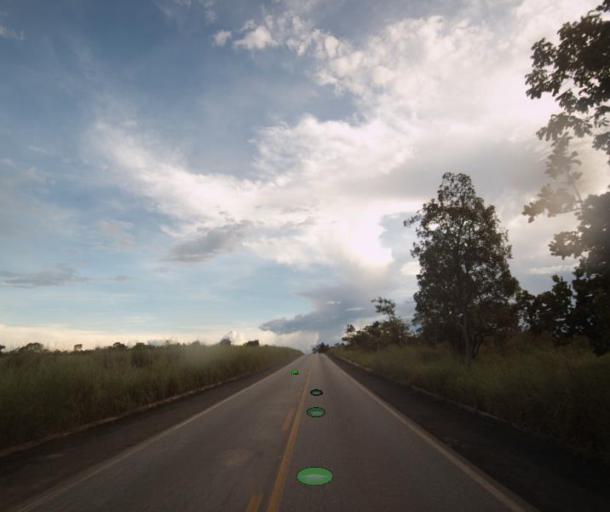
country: BR
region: Goias
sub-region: Uruacu
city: Uruacu
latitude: -14.0681
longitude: -49.0952
